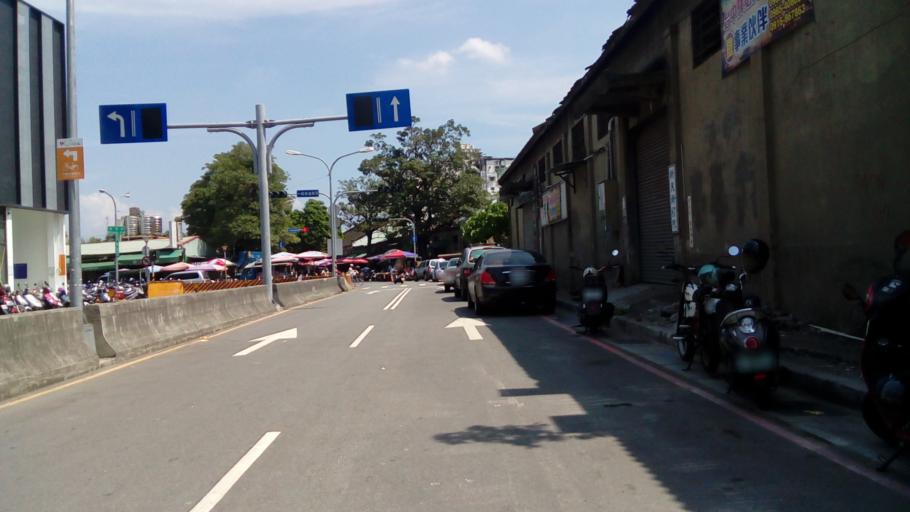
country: TW
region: Taiwan
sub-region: Taichung City
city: Taichung
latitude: 24.1379
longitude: 120.6871
